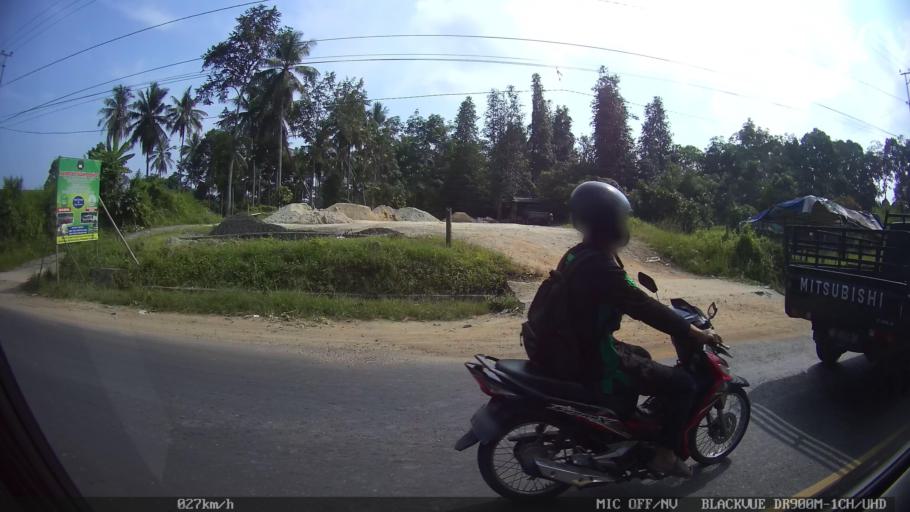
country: ID
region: Lampung
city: Gedongtataan
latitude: -5.3669
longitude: 105.1541
